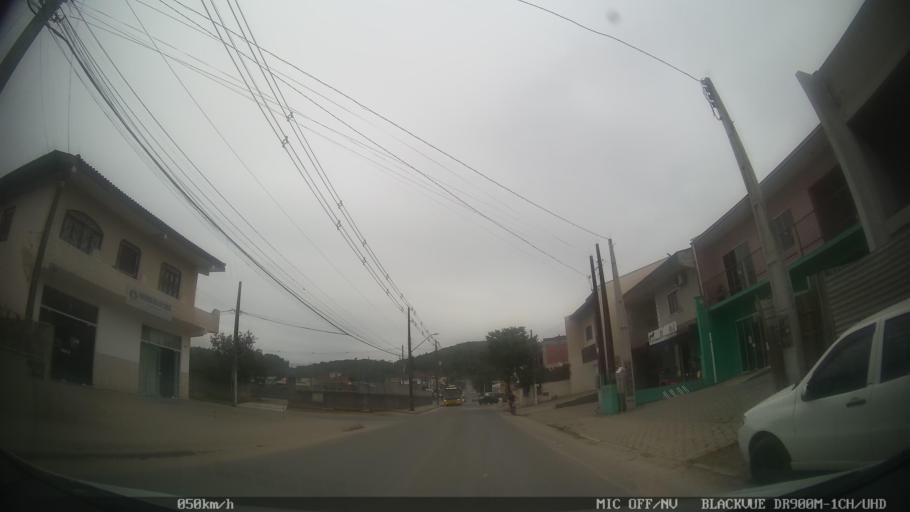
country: BR
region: Santa Catarina
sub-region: Joinville
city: Joinville
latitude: -26.3491
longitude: -48.7944
